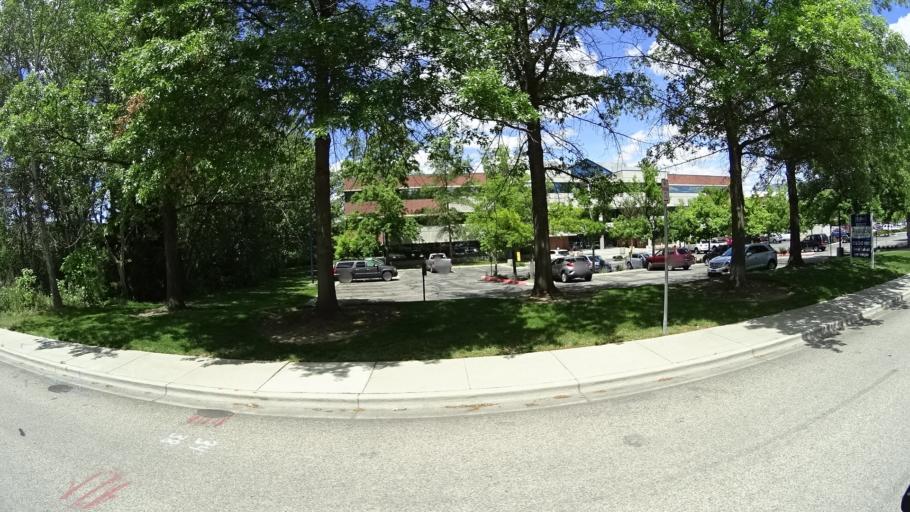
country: US
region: Idaho
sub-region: Ada County
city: Boise
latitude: 43.5960
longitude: -116.1801
